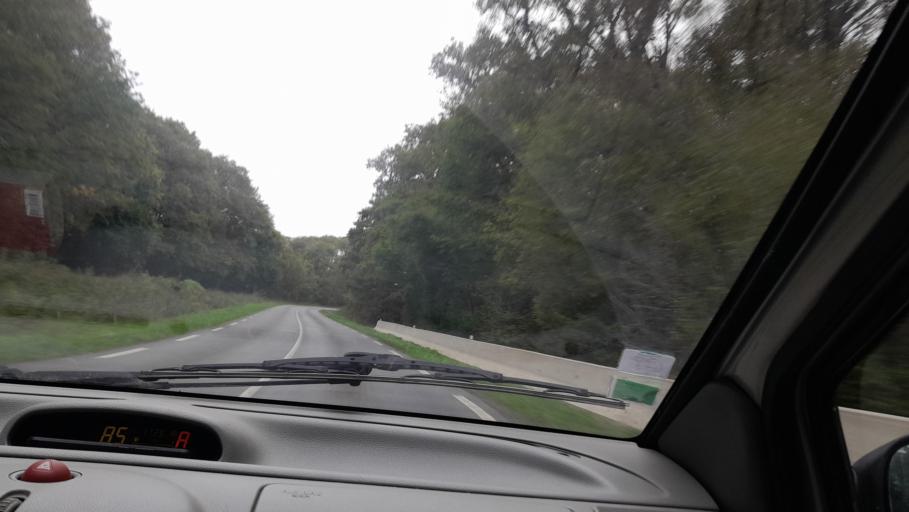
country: FR
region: Pays de la Loire
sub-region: Departement de Maine-et-Loire
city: Pouance
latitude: 47.6844
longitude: -1.1820
